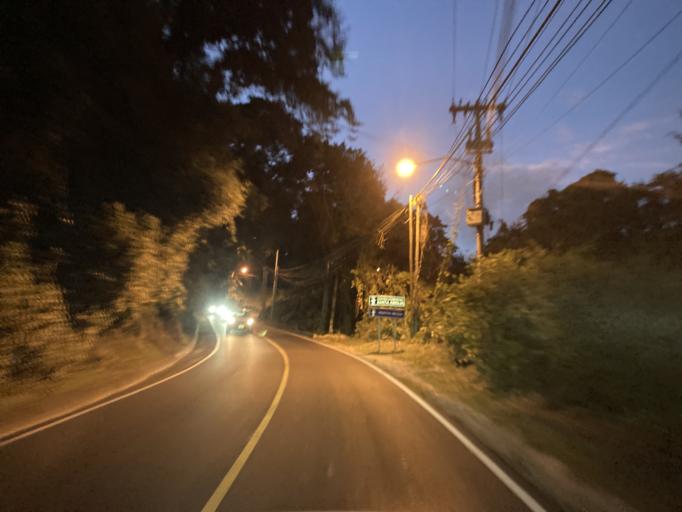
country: GT
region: Guatemala
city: Santa Catarina Pinula
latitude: 14.5974
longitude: -90.4659
